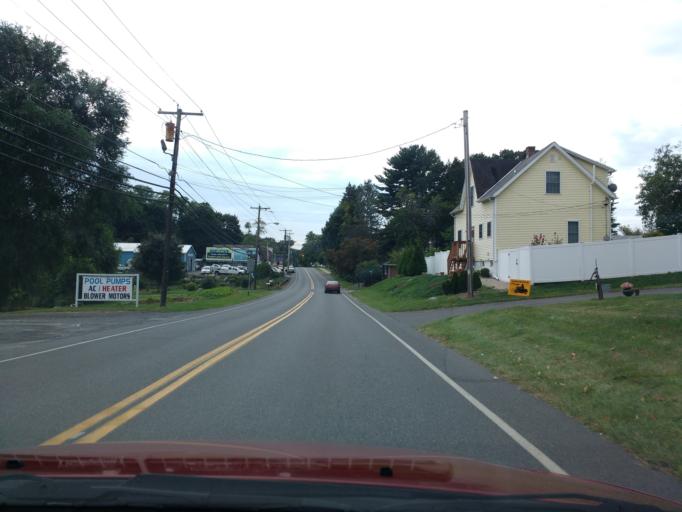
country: US
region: New York
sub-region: Ulster County
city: Lincoln Park
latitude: 41.9393
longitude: -73.9853
